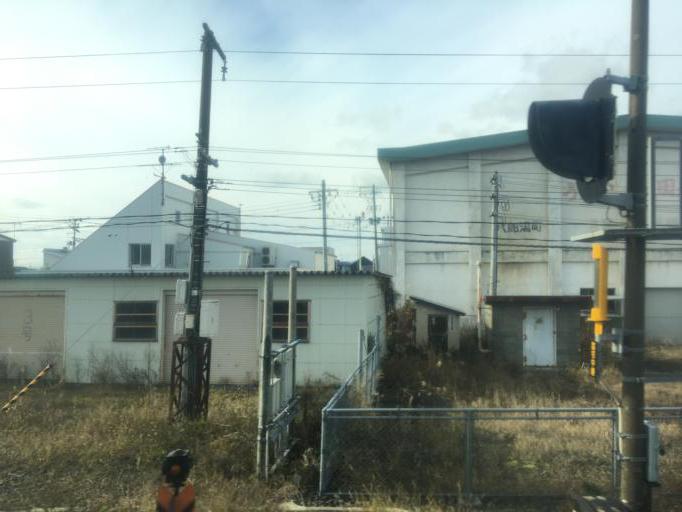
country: JP
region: Akita
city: Tenno
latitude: 39.9494
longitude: 140.0780
